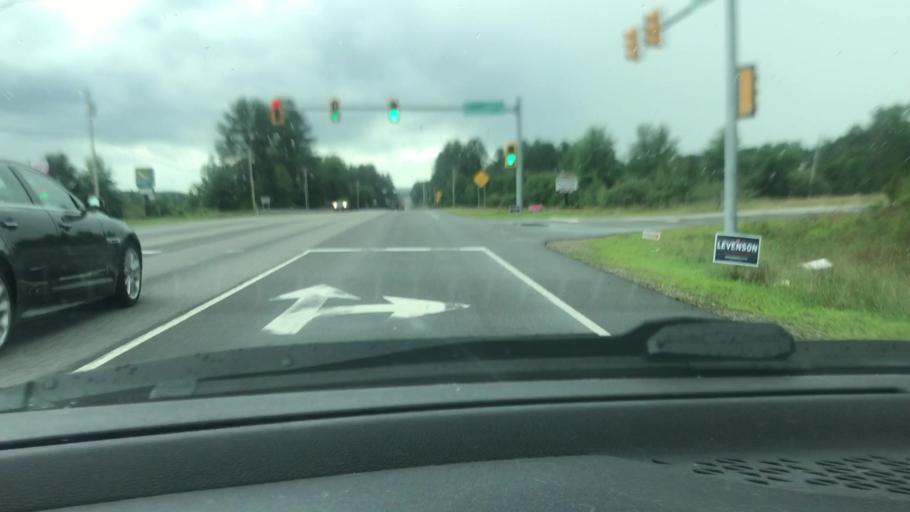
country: US
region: New Hampshire
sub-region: Merrimack County
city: Chichester
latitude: 43.2540
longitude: -71.4589
